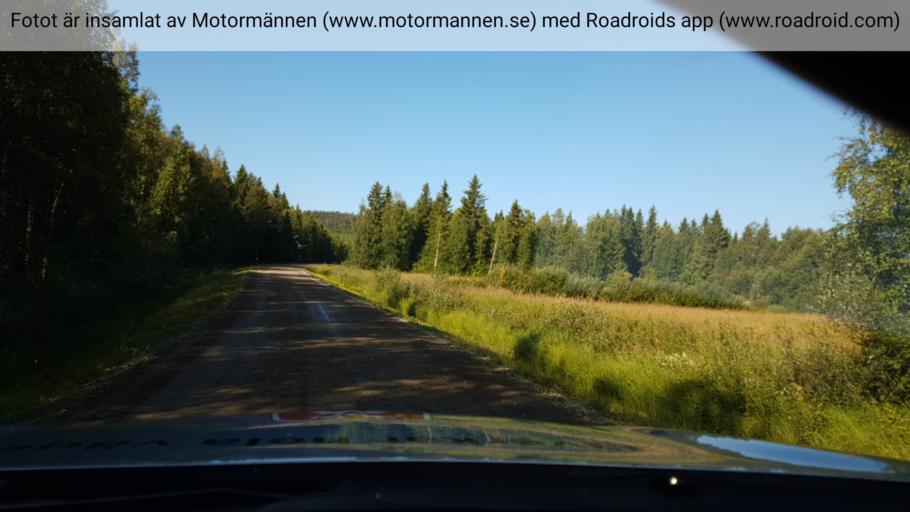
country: SE
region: Norrbotten
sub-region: Kalix Kommun
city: Kalix
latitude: 66.1828
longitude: 23.2083
